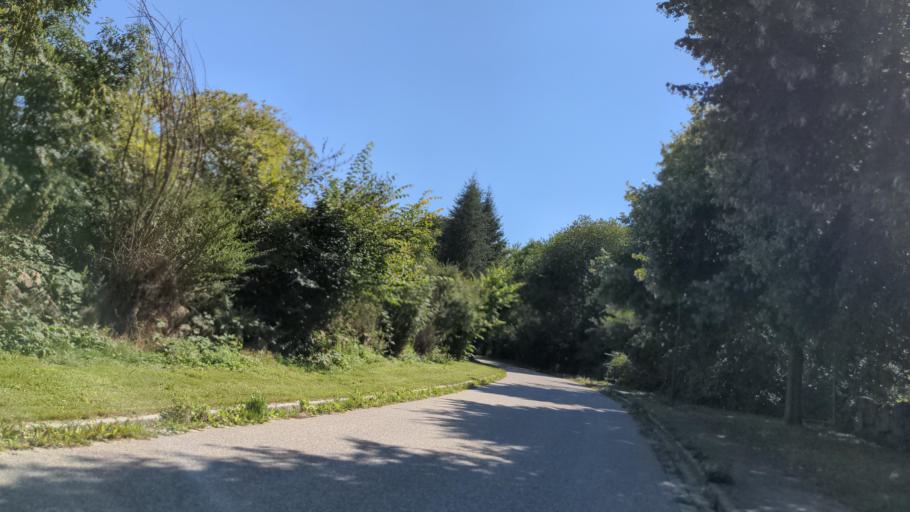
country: DE
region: Mecklenburg-Vorpommern
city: Selmsdorf
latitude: 53.8826
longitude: 10.8925
